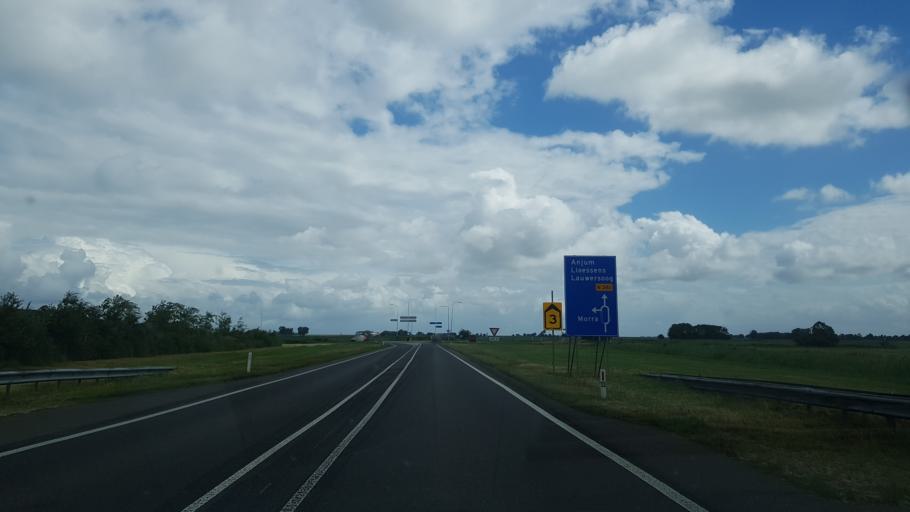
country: NL
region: Friesland
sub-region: Gemeente Dongeradeel
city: Anjum
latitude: 53.3688
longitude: 6.0898
